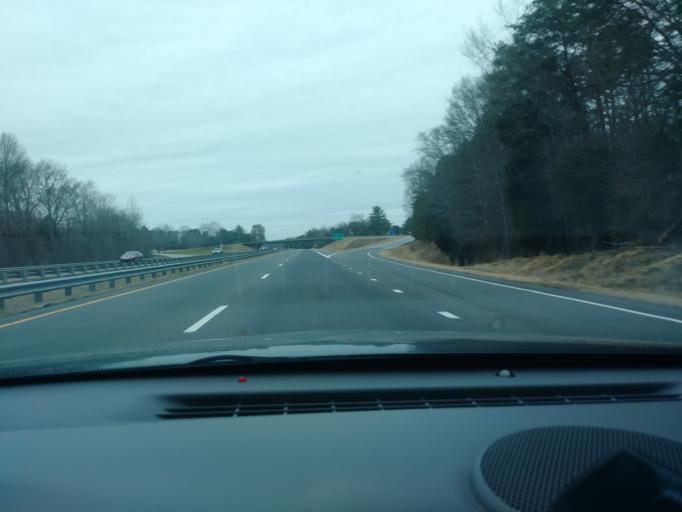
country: US
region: North Carolina
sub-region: Forsyth County
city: Lewisville
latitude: 36.0999
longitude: -80.4650
